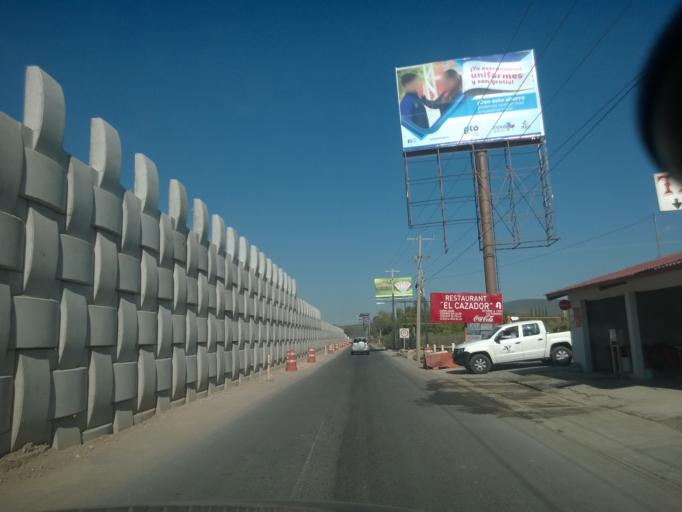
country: MX
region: Guanajuato
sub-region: Leon
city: Fraccionamiento Paseo de las Torres
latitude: 21.1921
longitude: -101.7482
